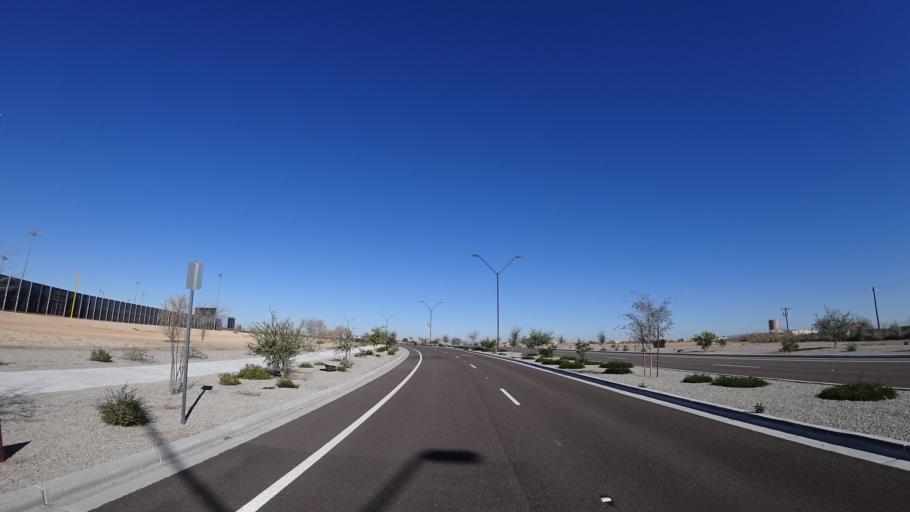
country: US
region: Arizona
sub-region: Maricopa County
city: Goodyear
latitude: 33.4140
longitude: -112.3892
